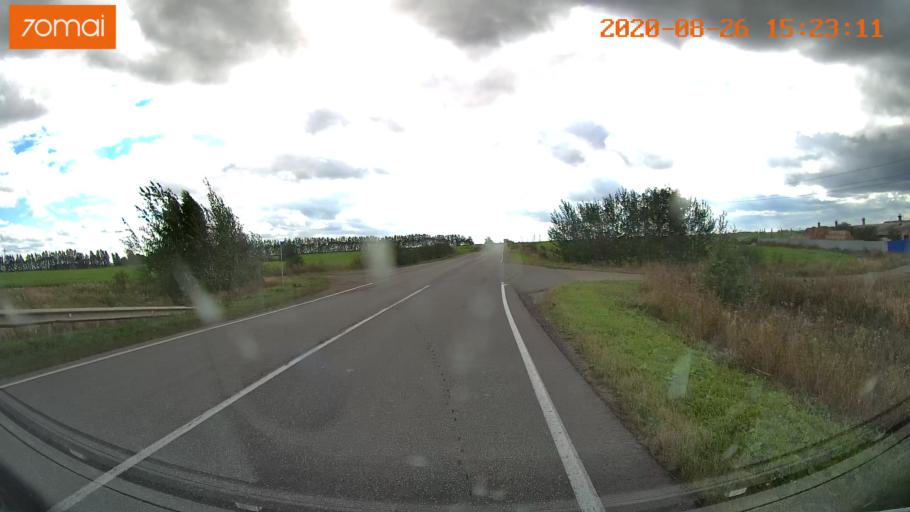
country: RU
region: Tula
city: Severo-Zadonsk
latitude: 54.1216
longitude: 38.4543
